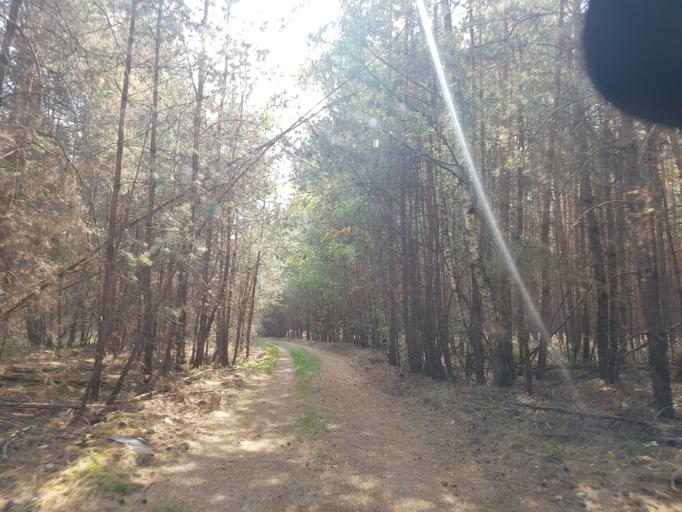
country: DE
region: Brandenburg
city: Treuenbrietzen
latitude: 52.0212
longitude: 12.8779
